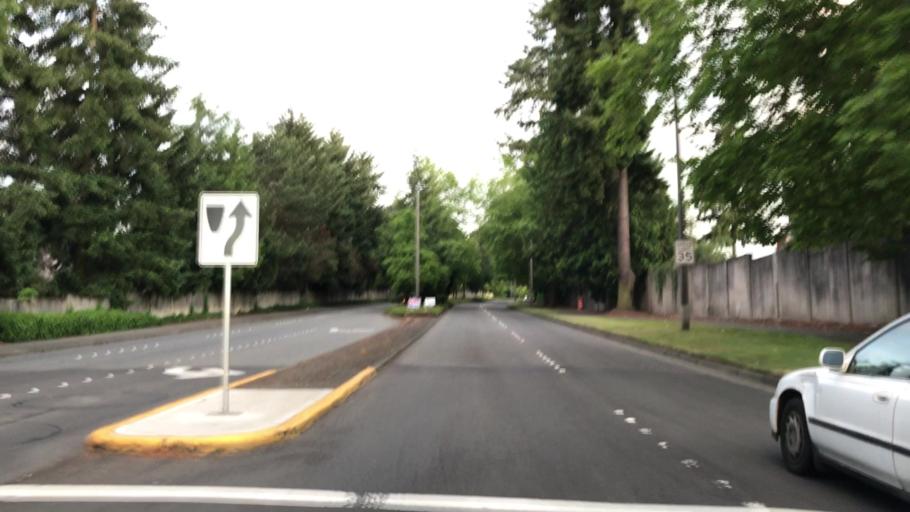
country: US
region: Washington
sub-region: King County
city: Eastgate
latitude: 47.6025
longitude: -122.1429
